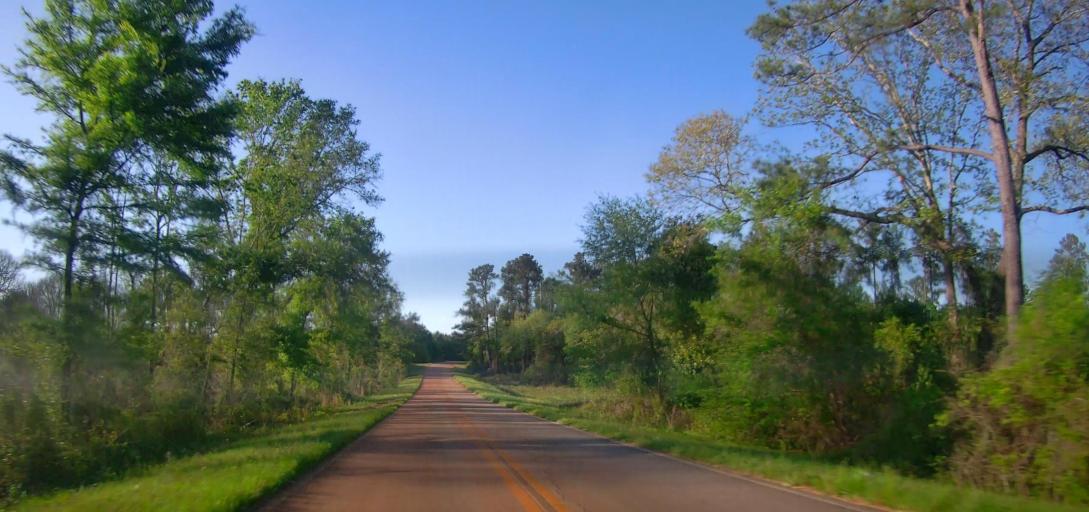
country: US
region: Georgia
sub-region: Macon County
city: Oglethorpe
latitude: 32.2888
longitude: -84.1468
